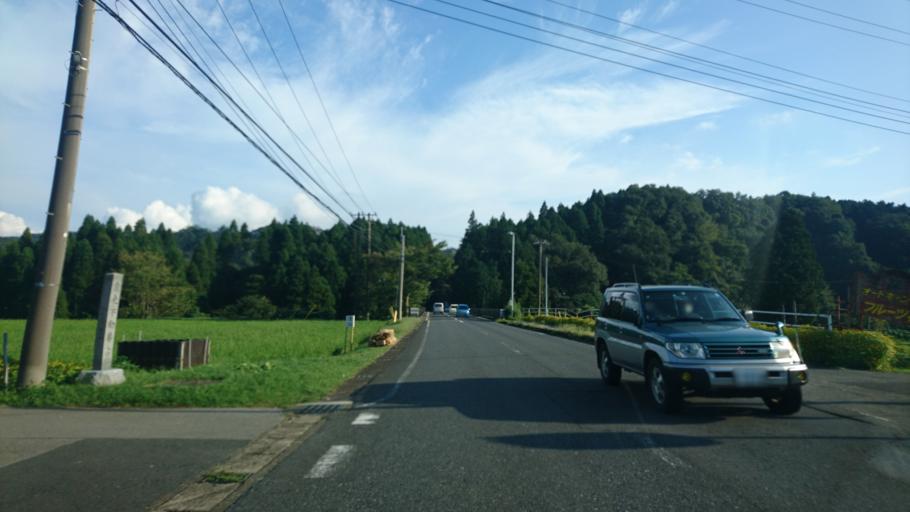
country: JP
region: Chiba
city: Kawaguchi
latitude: 35.2042
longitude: 140.0216
